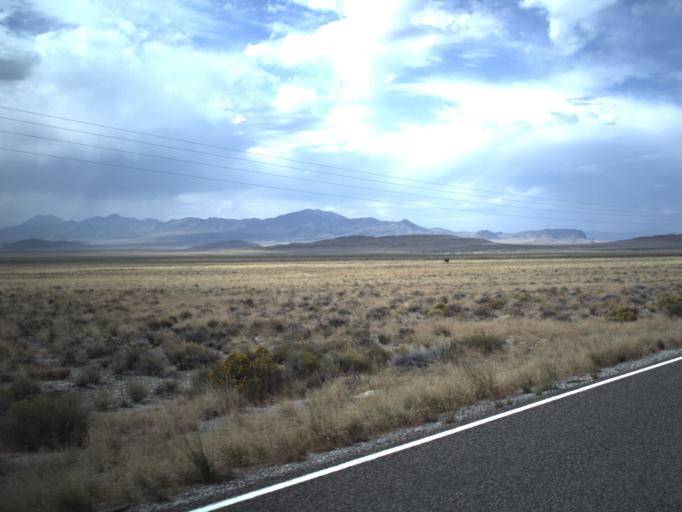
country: US
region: Utah
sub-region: Tooele County
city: Wendover
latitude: 41.4298
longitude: -113.8102
